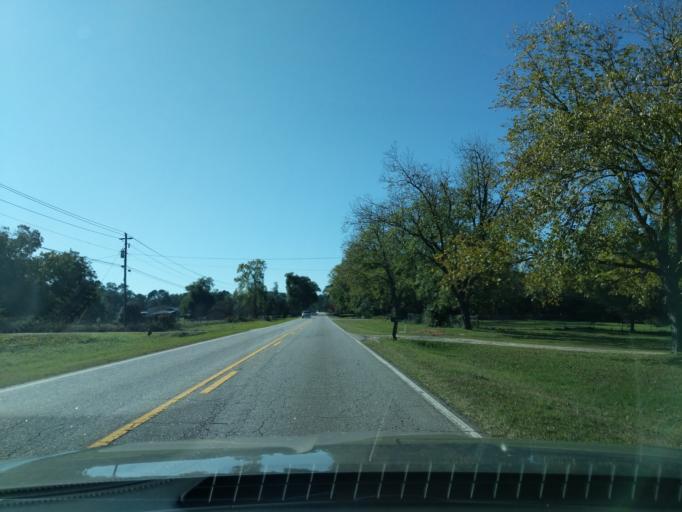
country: US
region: Georgia
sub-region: Columbia County
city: Grovetown
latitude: 33.4658
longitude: -82.1671
